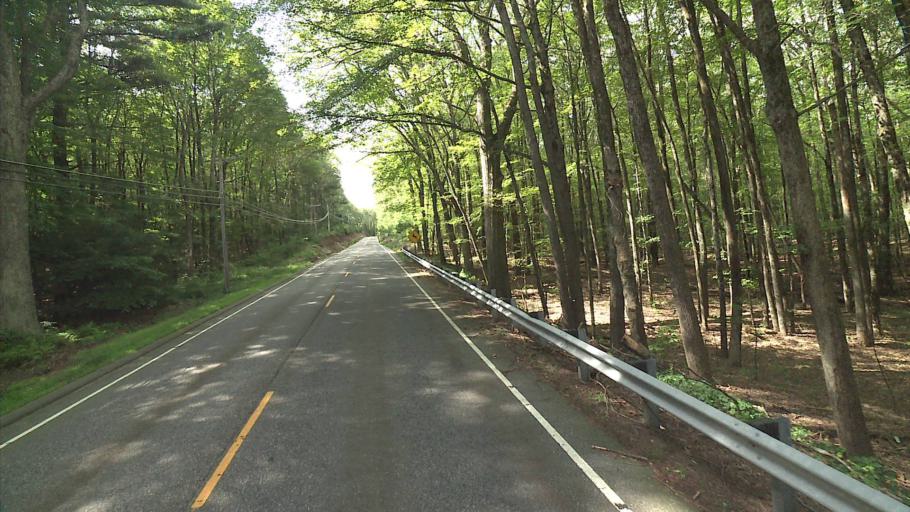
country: US
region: Massachusetts
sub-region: Hampden County
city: Holland
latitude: 42.0047
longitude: -72.1487
